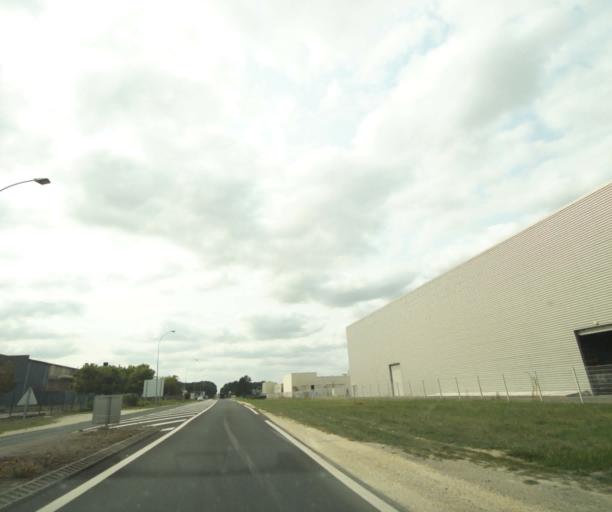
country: FR
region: Centre
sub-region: Departement de l'Indre
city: Buzancais
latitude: 46.8910
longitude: 1.4009
